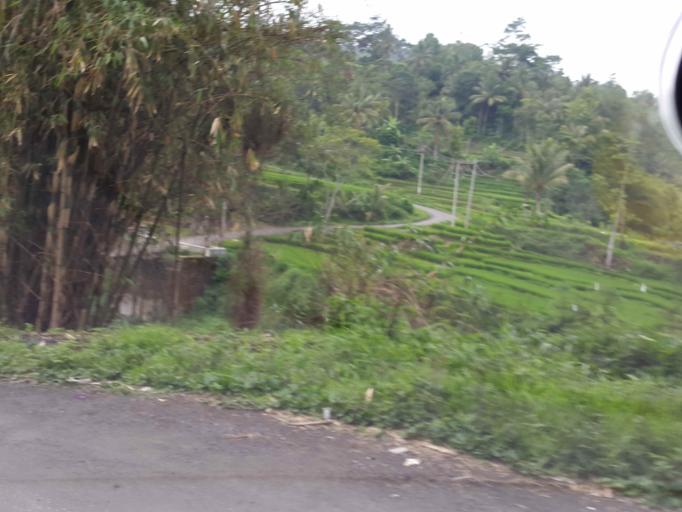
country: ID
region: Central Java
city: Lebaksiu
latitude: -7.1176
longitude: 109.1536
